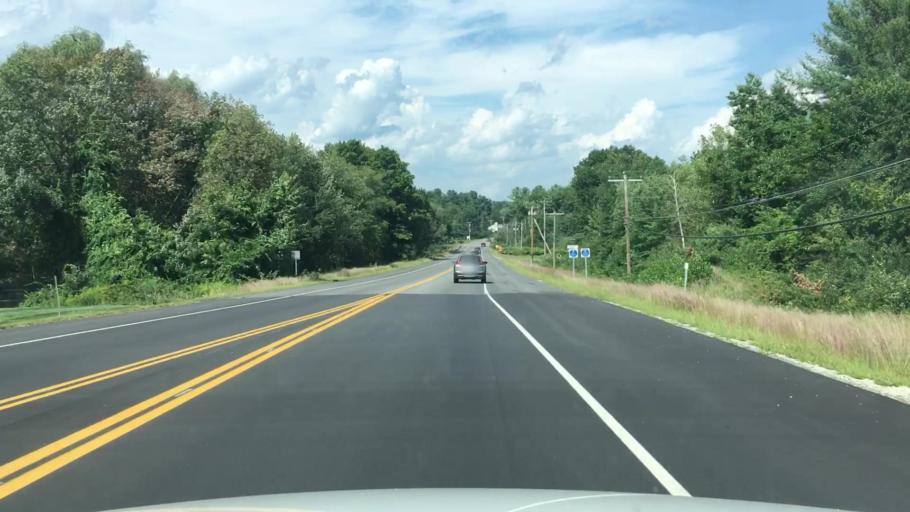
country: US
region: New Hampshire
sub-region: Rockingham County
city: Londonderry
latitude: 42.8529
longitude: -71.3570
